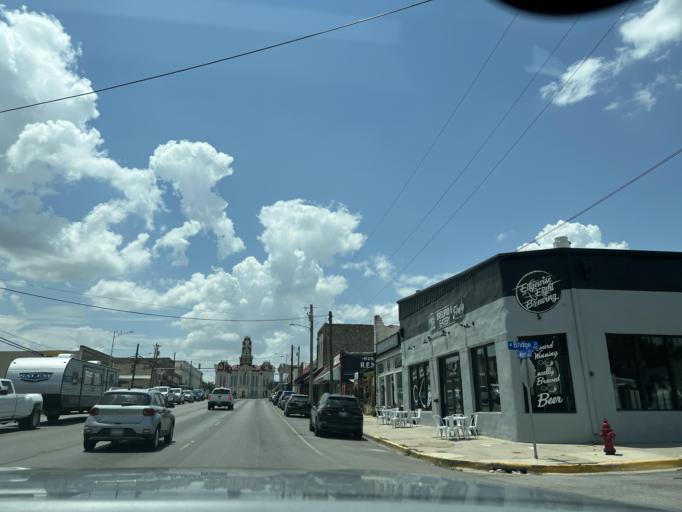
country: US
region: Texas
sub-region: Parker County
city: Weatherford
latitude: 32.7616
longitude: -97.7974
